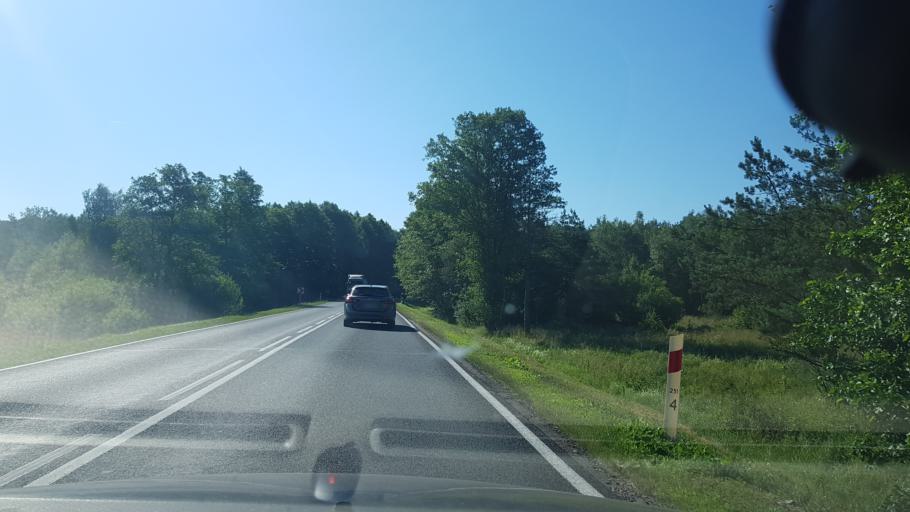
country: PL
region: Masovian Voivodeship
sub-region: Powiat wyszkowski
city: Branszczyk
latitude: 52.5809
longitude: 21.5321
